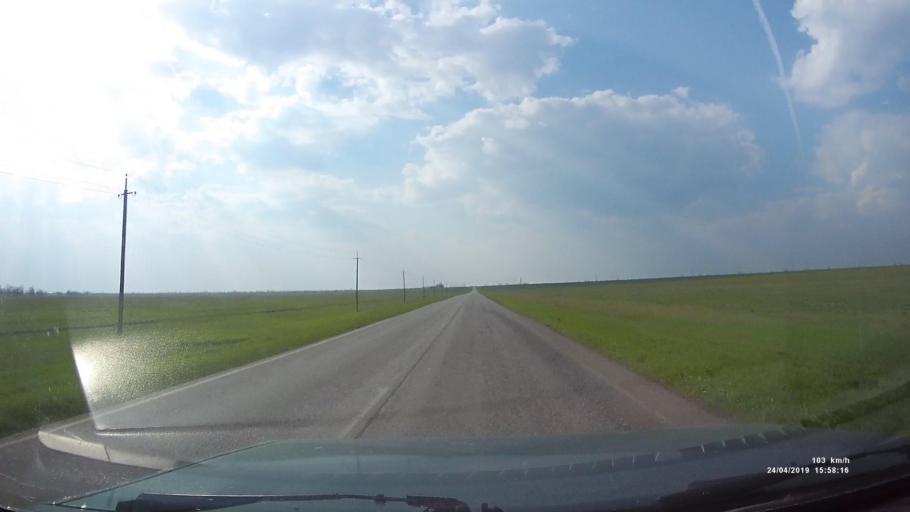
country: RU
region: Kalmykiya
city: Yashalta
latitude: 46.6125
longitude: 42.4935
